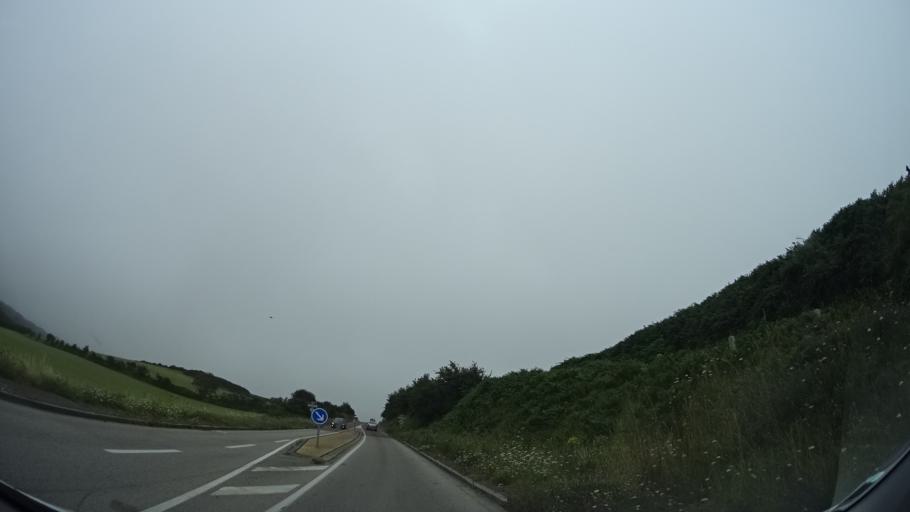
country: FR
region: Lower Normandy
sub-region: Departement de la Manche
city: Flamanville
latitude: 49.5501
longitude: -1.8564
